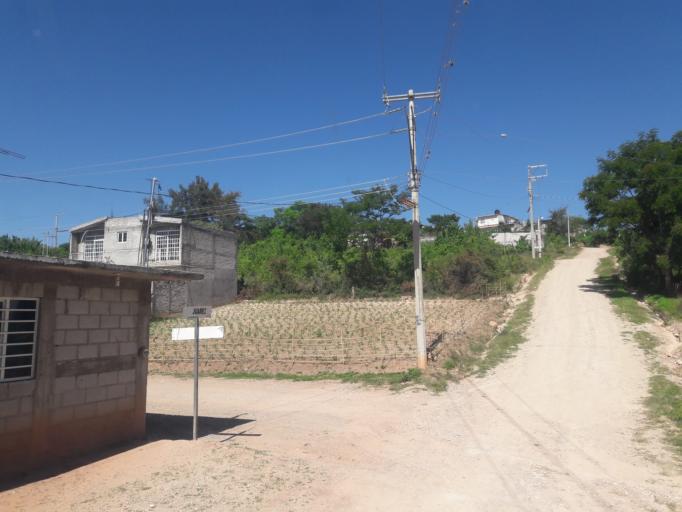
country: MX
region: Oaxaca
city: Ciudad de Huajuapam de Leon
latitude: 17.8009
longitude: -97.8018
